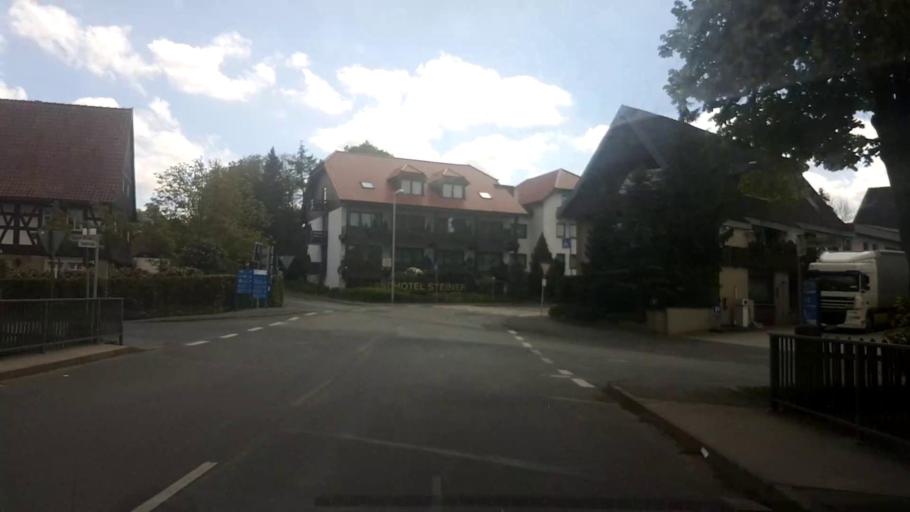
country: DE
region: Bavaria
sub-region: Upper Franconia
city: Grossheirath
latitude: 50.1773
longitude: 10.9492
